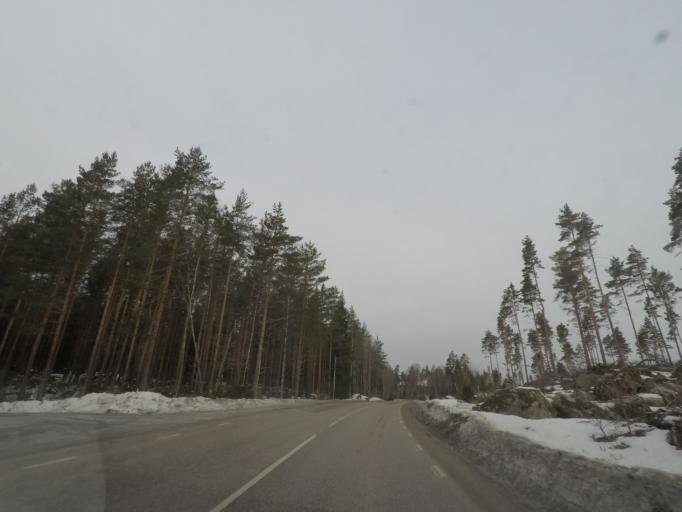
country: SE
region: Vaestmanland
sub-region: Vasteras
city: Skultuna
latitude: 59.7390
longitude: 16.3983
